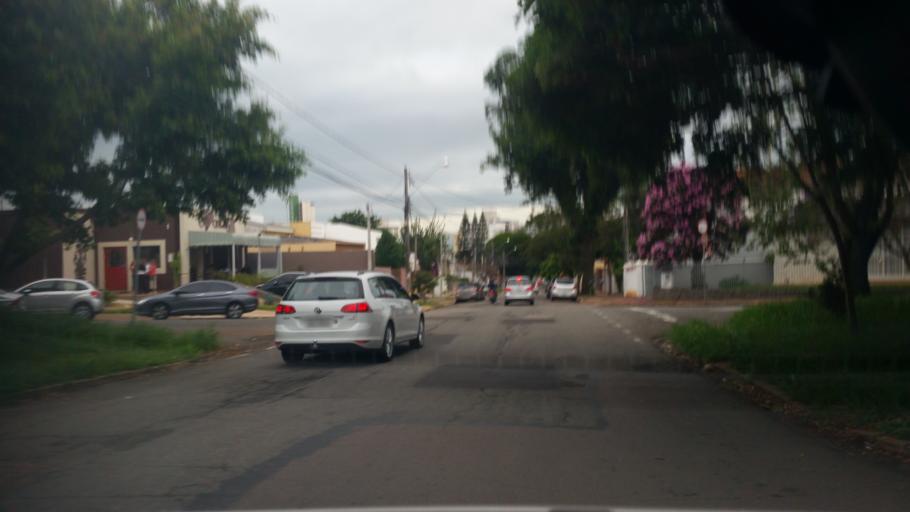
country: BR
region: Sao Paulo
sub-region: Campinas
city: Campinas
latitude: -22.8873
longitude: -47.0712
